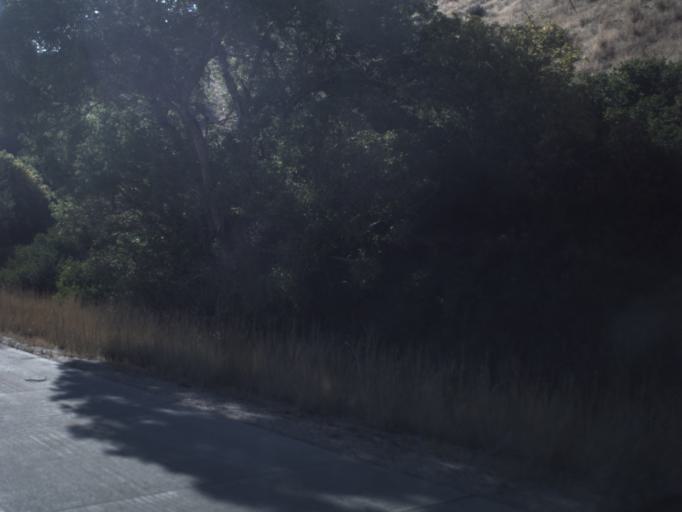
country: US
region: Utah
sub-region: Morgan County
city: Morgan
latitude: 41.0424
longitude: -111.6585
